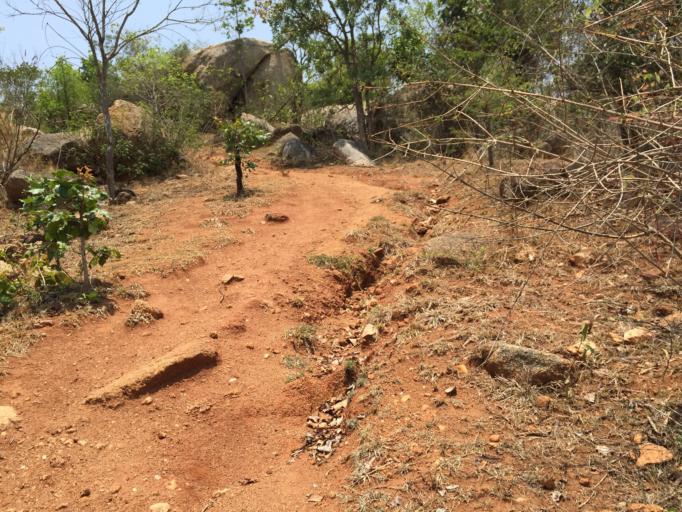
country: IN
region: Karnataka
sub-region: Bangalore Urban
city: Bangalore
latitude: 12.8885
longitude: 77.5288
